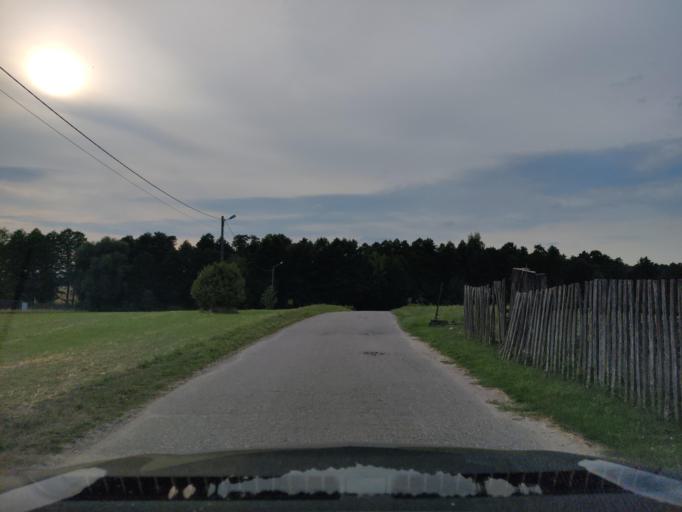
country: PL
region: Masovian Voivodeship
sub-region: Powiat pultuski
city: Obryte
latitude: 52.7412
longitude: 21.2516
